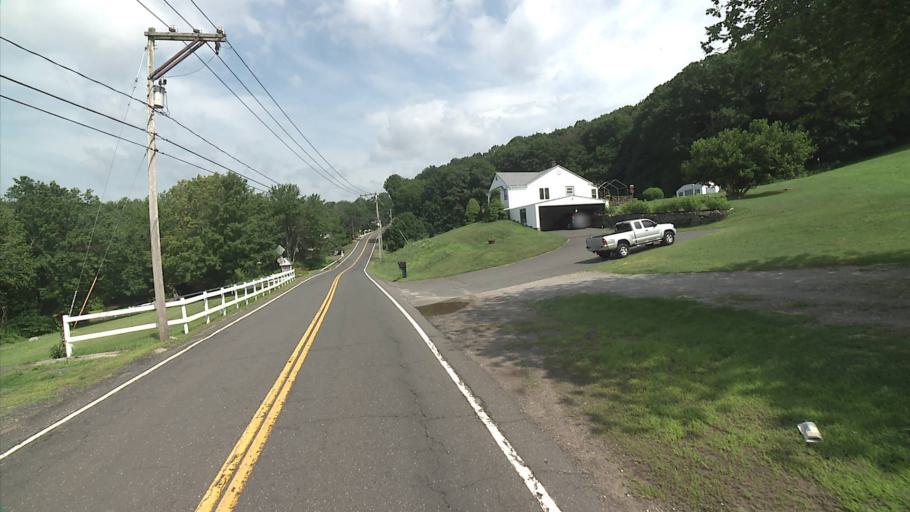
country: US
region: Connecticut
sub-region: New Haven County
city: Wolcott
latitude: 41.5975
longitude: -72.9646
